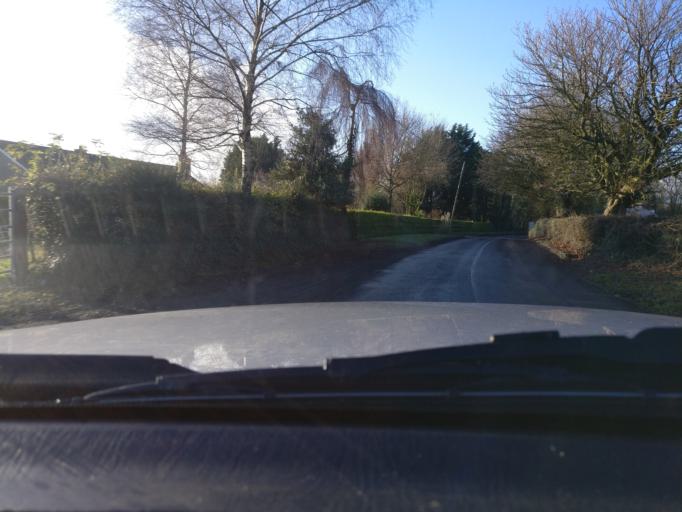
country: IE
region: Leinster
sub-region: An Mhi
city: Athboy
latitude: 53.6723
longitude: -6.9697
